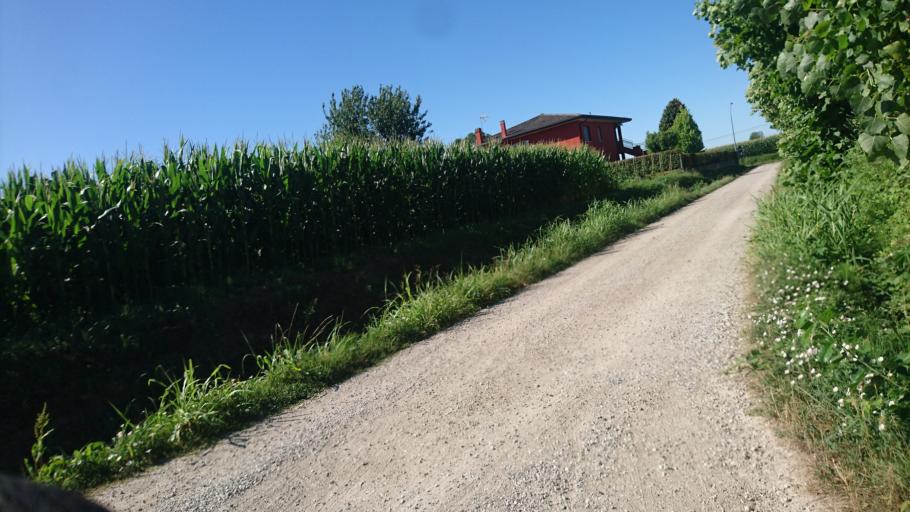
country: IT
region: Veneto
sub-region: Provincia di Padova
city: Legnaro
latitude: 45.3333
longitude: 11.9671
